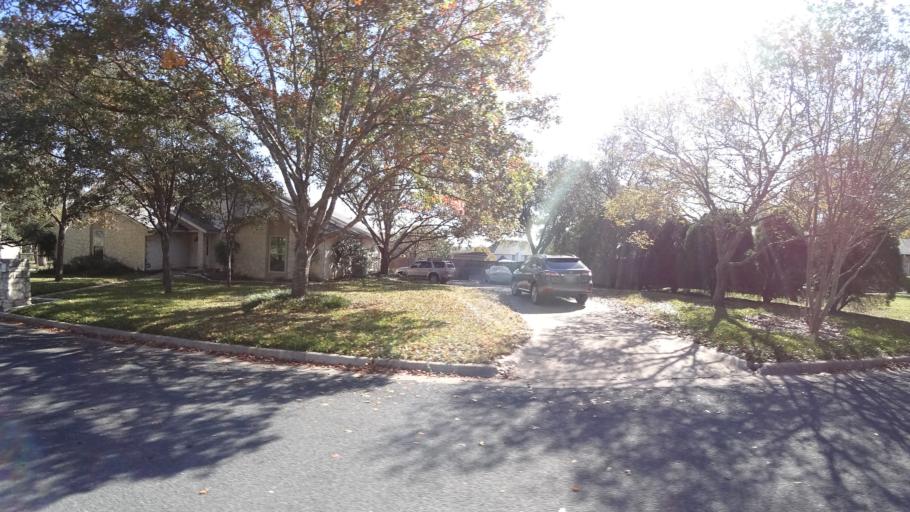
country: US
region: Texas
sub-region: Travis County
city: Barton Creek
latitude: 30.2308
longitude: -97.8697
